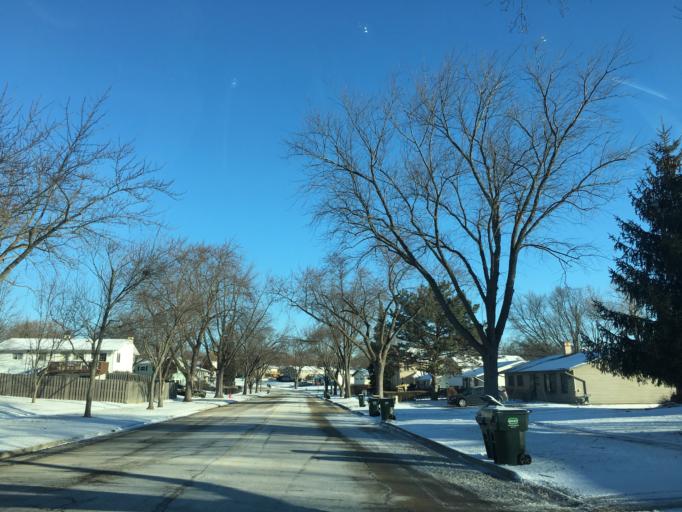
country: US
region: Illinois
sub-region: Cook County
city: Hoffman Estates
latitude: 42.0554
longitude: -88.0914
